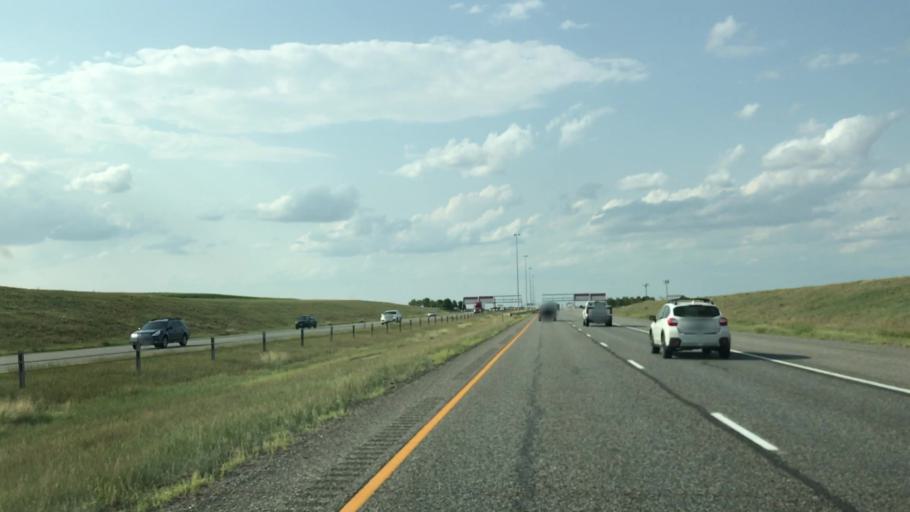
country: US
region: Colorado
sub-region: Adams County
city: Aurora
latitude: 39.6629
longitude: -104.7219
